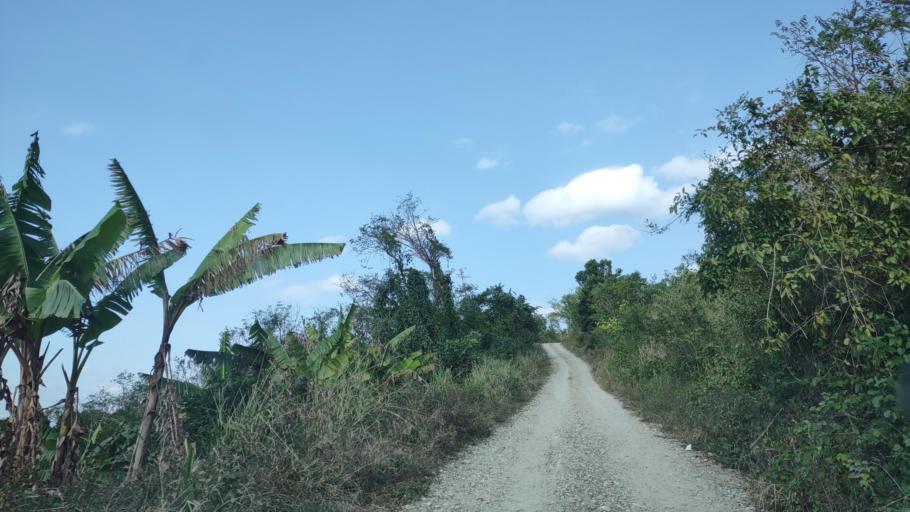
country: MX
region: Veracruz
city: Papantla de Olarte
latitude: 20.4581
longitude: -97.3959
